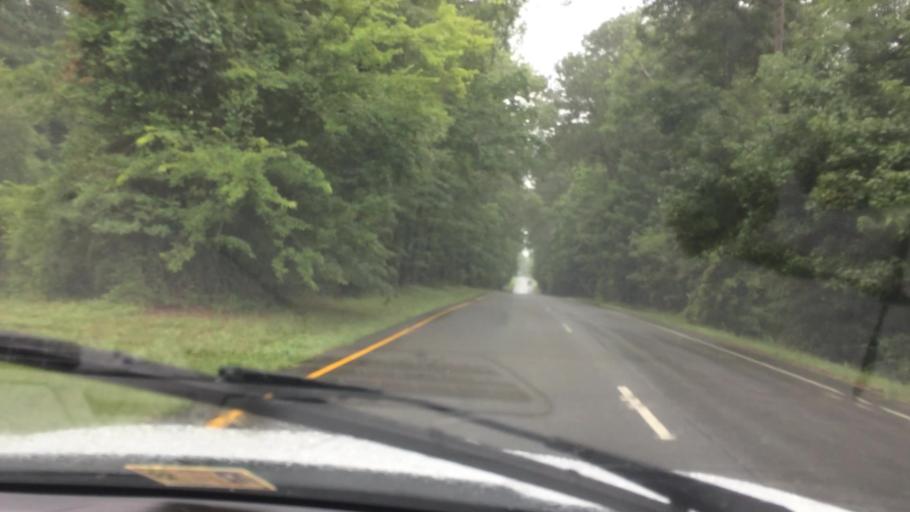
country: US
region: Virginia
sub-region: King William County
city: West Point
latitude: 37.5113
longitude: -76.8470
